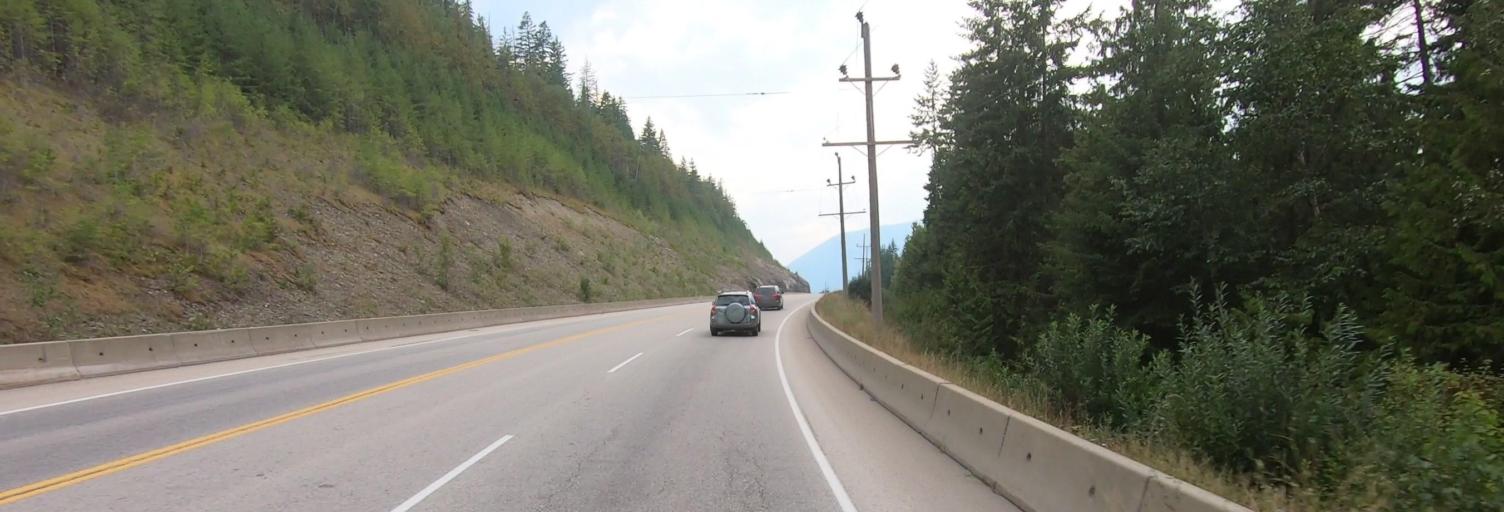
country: CA
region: British Columbia
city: Sicamous
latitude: 50.8308
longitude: -119.0092
